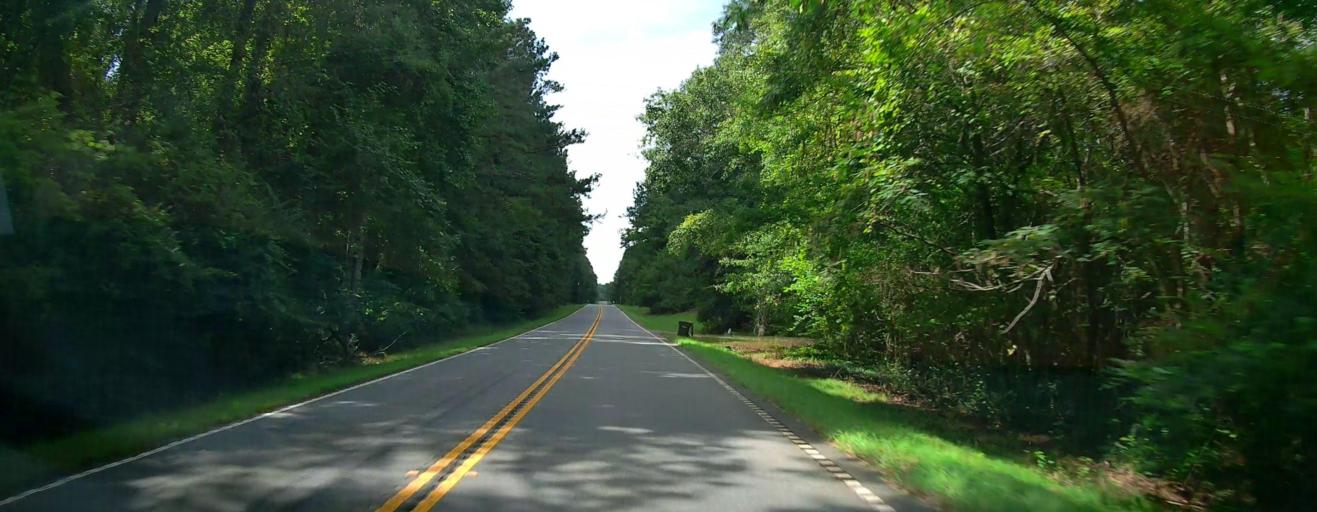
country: US
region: Georgia
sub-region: Talbot County
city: Talbotton
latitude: 32.6673
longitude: -84.5197
